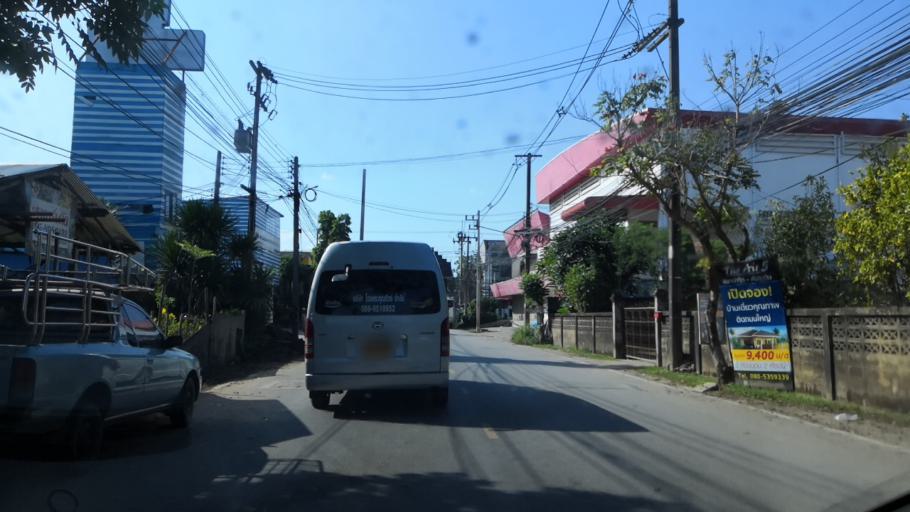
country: TH
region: Chiang Rai
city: Chiang Rai
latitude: 19.9291
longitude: 99.8456
